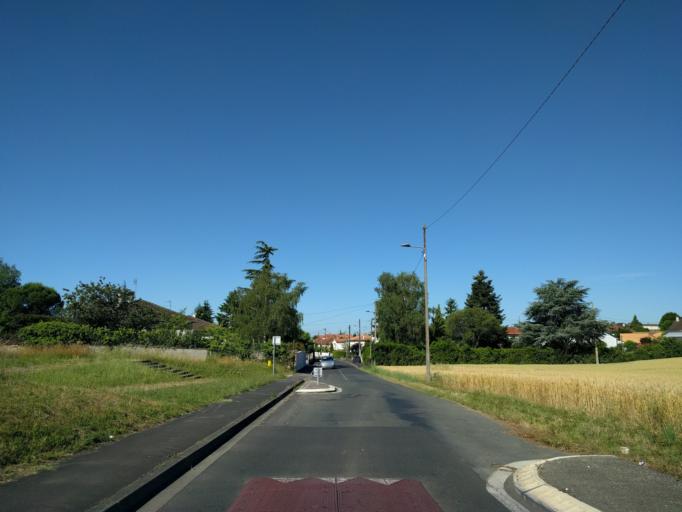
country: FR
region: Poitou-Charentes
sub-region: Departement des Deux-Sevres
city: Niort
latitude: 46.3367
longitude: -0.4255
